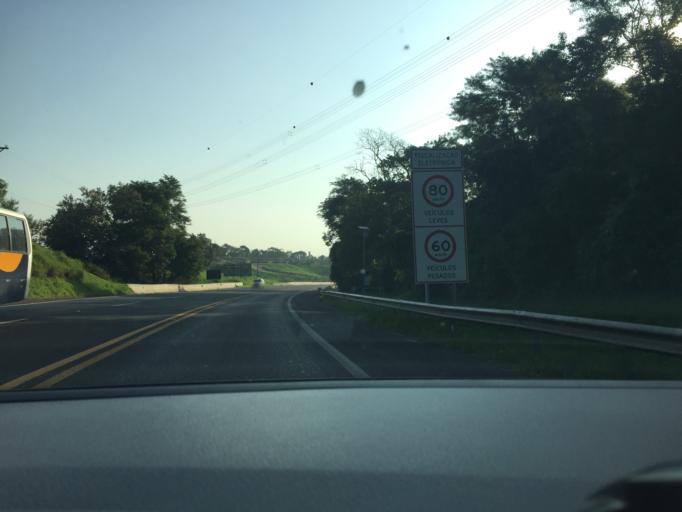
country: BR
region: Sao Paulo
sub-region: Louveira
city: Louveira
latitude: -23.0788
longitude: -46.9085
